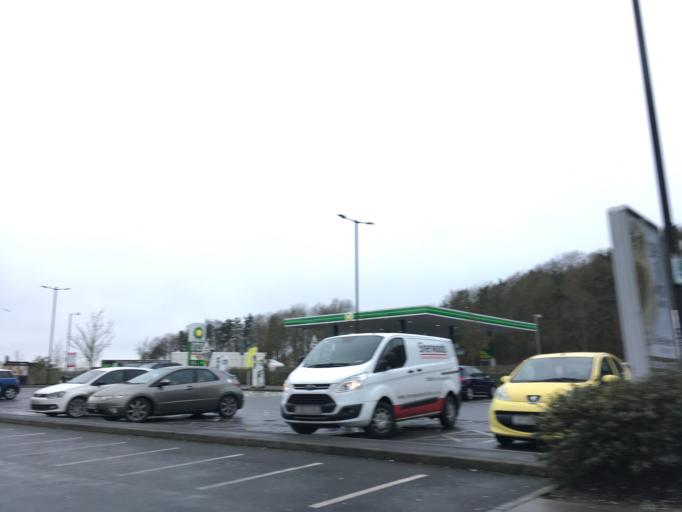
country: GB
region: England
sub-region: South Gloucestershire
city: Charfield
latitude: 51.6587
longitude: -2.4275
